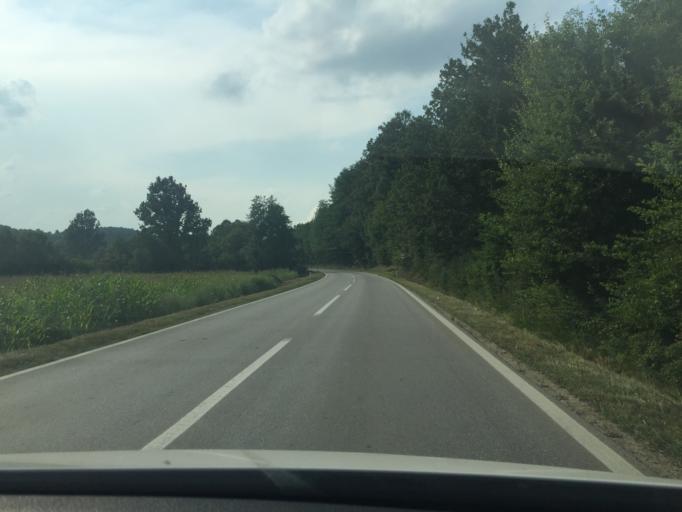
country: BA
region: Federation of Bosnia and Herzegovina
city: Mionica
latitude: 44.8198
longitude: 18.4637
